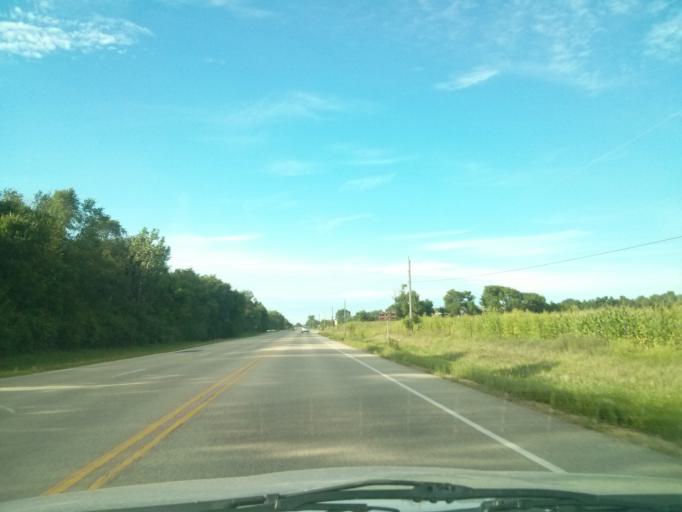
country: US
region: Minnesota
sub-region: Washington County
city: Lake Saint Croix Beach
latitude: 44.9360
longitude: -92.7316
